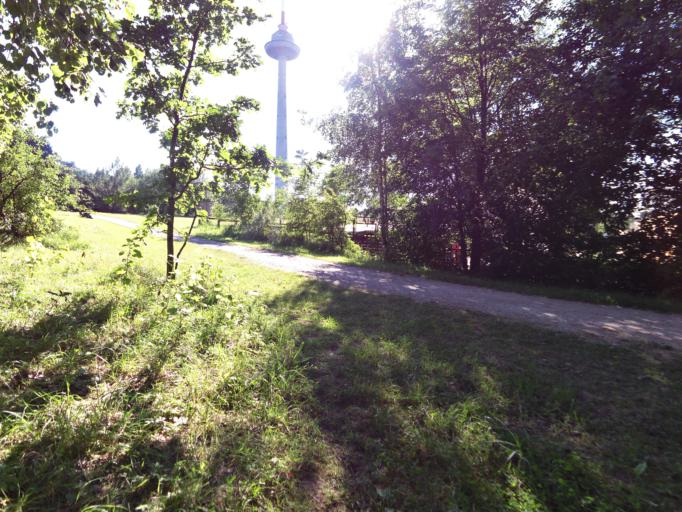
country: LT
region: Vilnius County
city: Lazdynai
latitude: 54.6887
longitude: 25.2192
